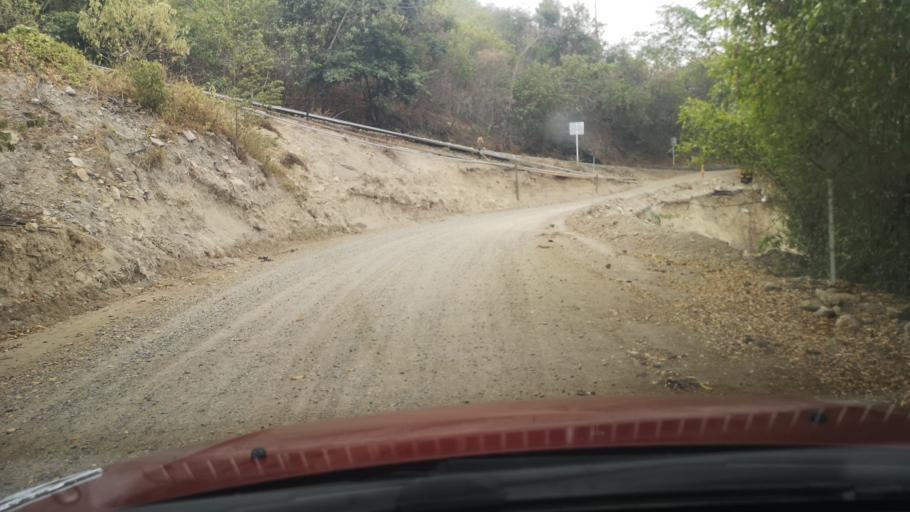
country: CO
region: Huila
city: Neiva
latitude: 2.9579
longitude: -75.3498
